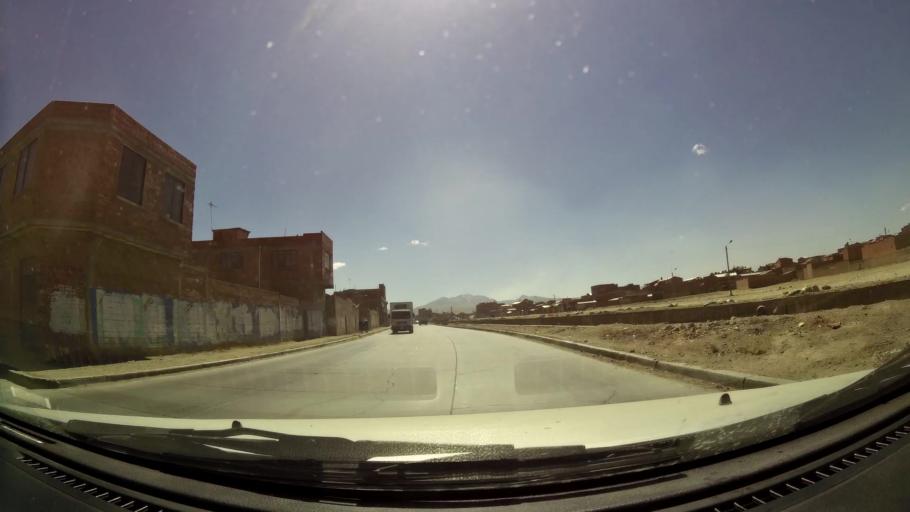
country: BO
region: La Paz
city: La Paz
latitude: -16.5034
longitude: -68.2100
